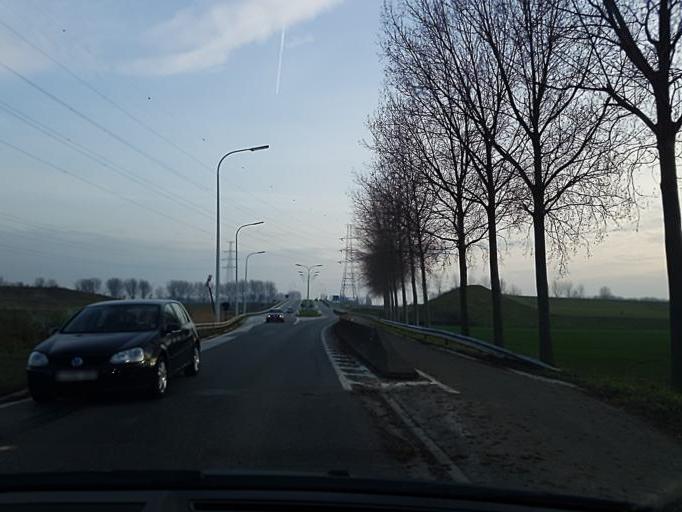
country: BE
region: Flanders
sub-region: Provincie Oost-Vlaanderen
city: Beveren
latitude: 51.2460
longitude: 4.2741
